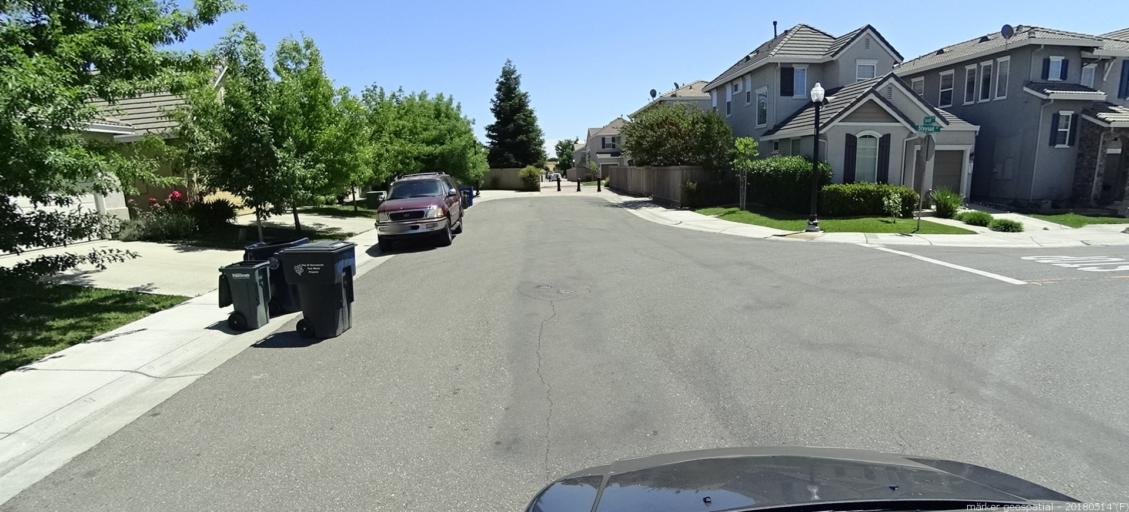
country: US
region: California
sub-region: Yolo County
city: West Sacramento
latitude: 38.6273
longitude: -121.5229
